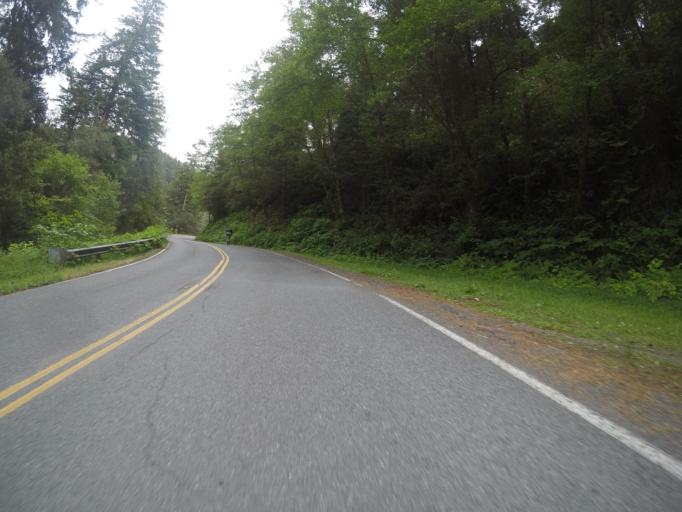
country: US
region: California
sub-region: Del Norte County
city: Bertsch-Oceanview
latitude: 41.7779
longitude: -124.0149
